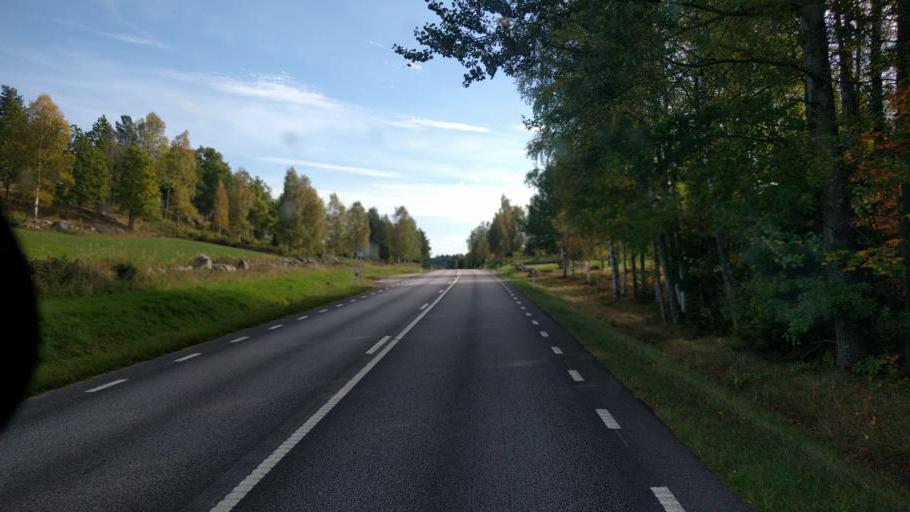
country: SE
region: OEstergoetland
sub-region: Kinda Kommun
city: Kisa
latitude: 57.9204
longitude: 15.6791
